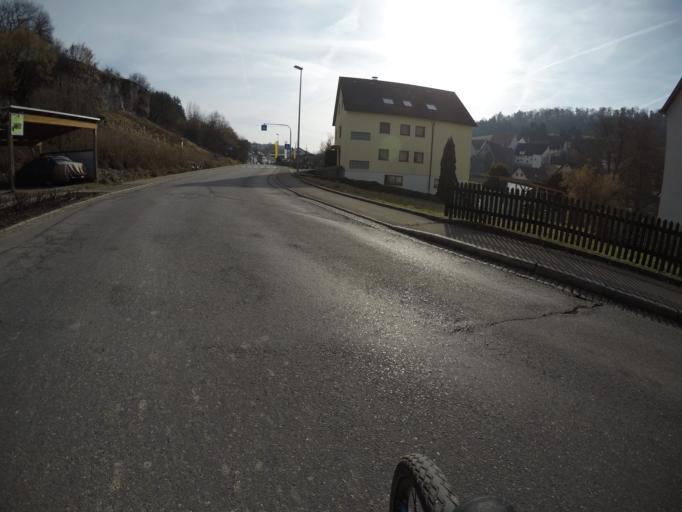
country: DE
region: Baden-Wuerttemberg
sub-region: Karlsruhe Region
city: Wildberg
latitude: 48.6207
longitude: 8.7769
